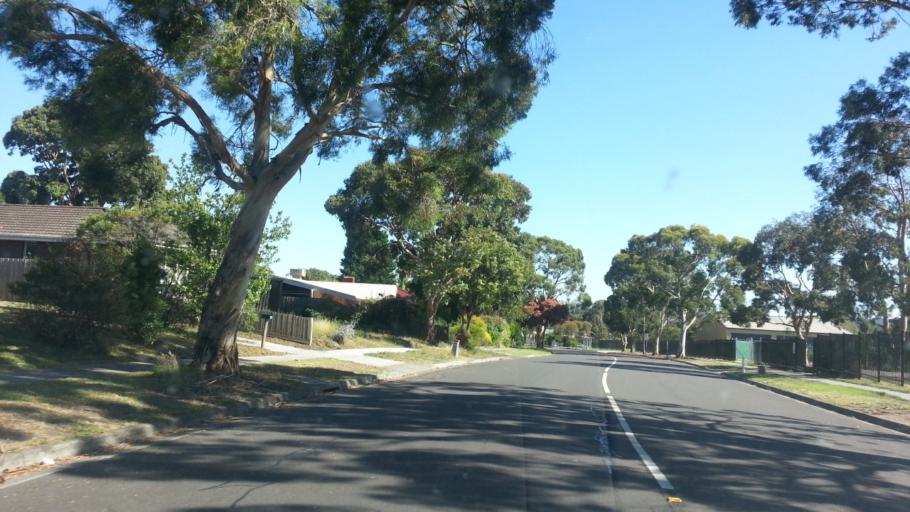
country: AU
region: Victoria
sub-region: Knox
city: Rowville
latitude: -37.9204
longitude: 145.2627
